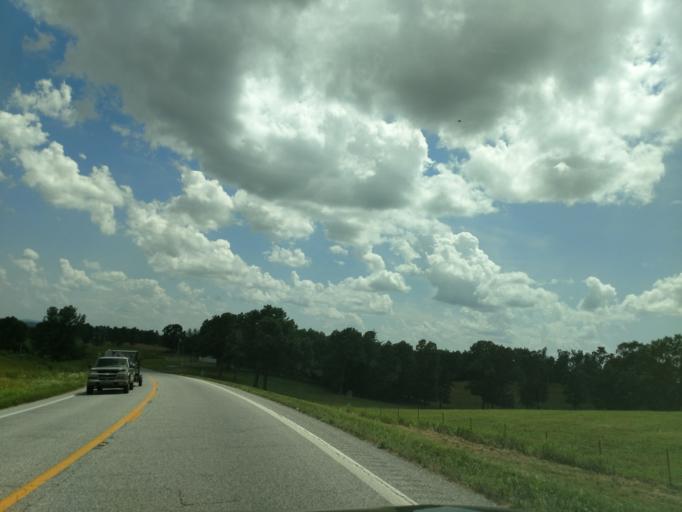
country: US
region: Arkansas
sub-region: Boone County
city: Harrison
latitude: 36.2092
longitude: -92.9334
